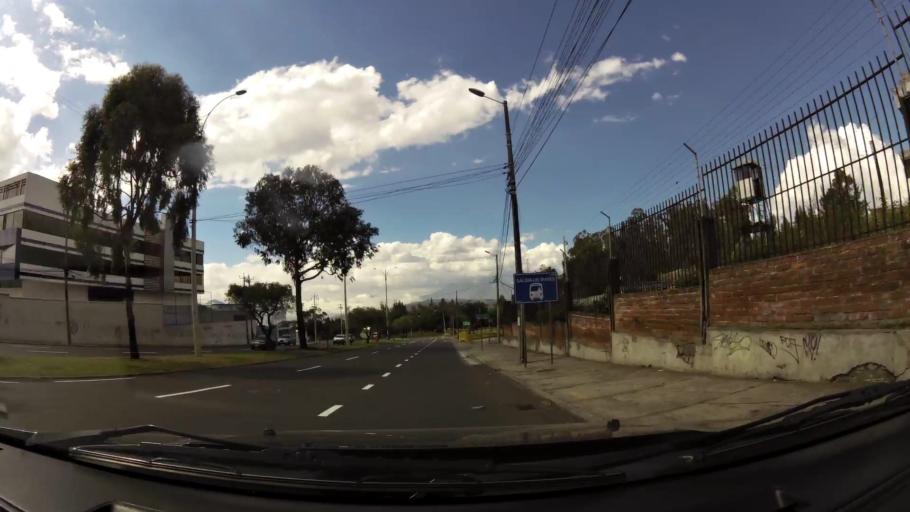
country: EC
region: Pichincha
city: Quito
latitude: -0.0992
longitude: -78.4709
